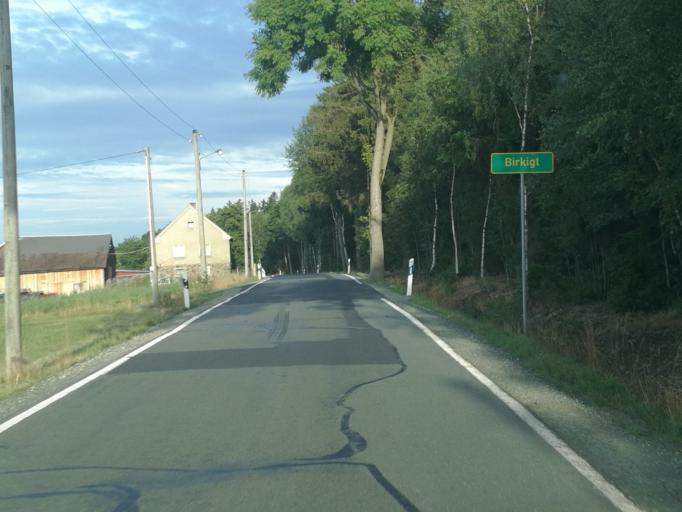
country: DE
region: Saxony
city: Triebel
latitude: 50.3353
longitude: 12.1142
